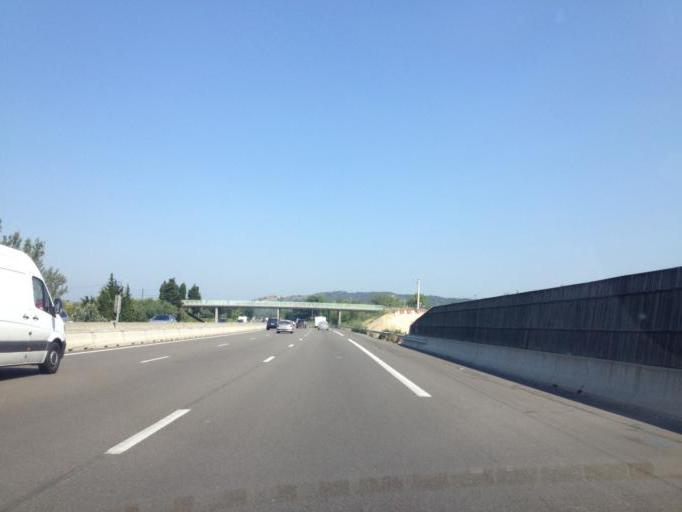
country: FR
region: Provence-Alpes-Cote d'Azur
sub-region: Departement du Vaucluse
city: Piolenc
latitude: 44.1830
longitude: 4.7519
